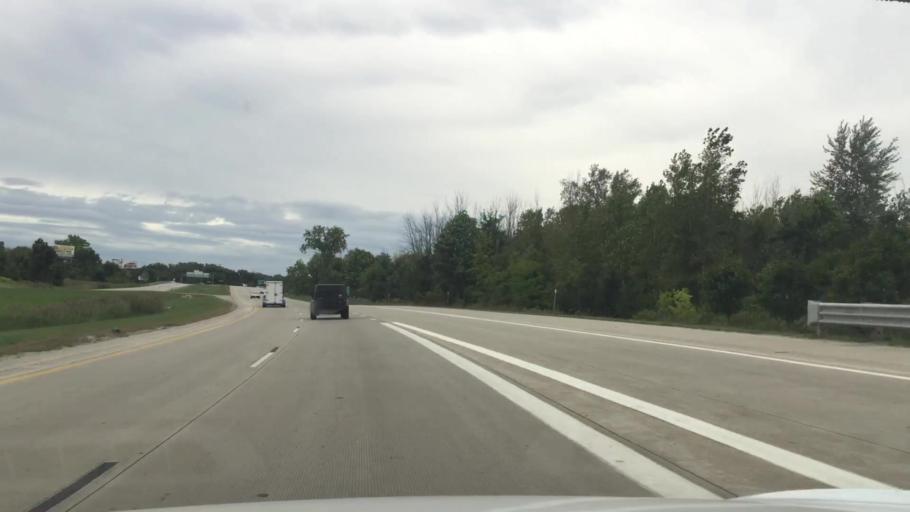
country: US
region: Michigan
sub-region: Saint Clair County
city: Port Huron
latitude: 42.9849
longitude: -82.4749
